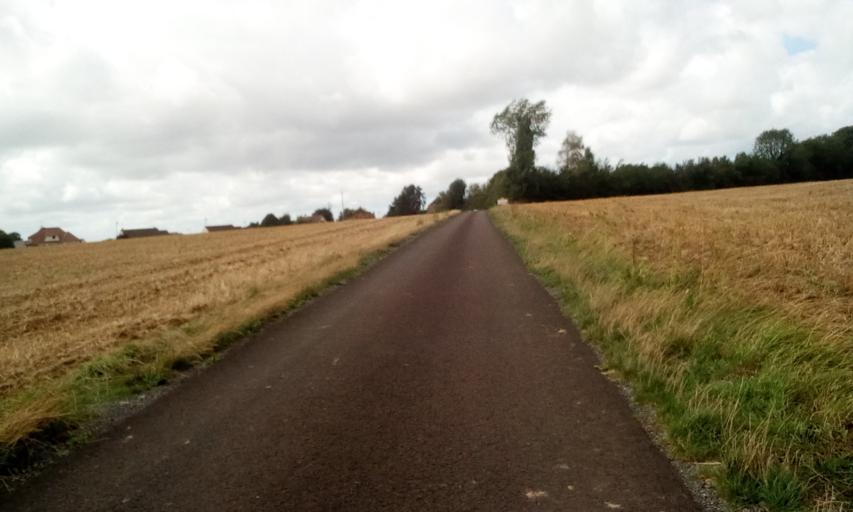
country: FR
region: Lower Normandy
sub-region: Departement du Calvados
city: Tilly-sur-Seulles
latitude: 49.2332
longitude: -0.6168
